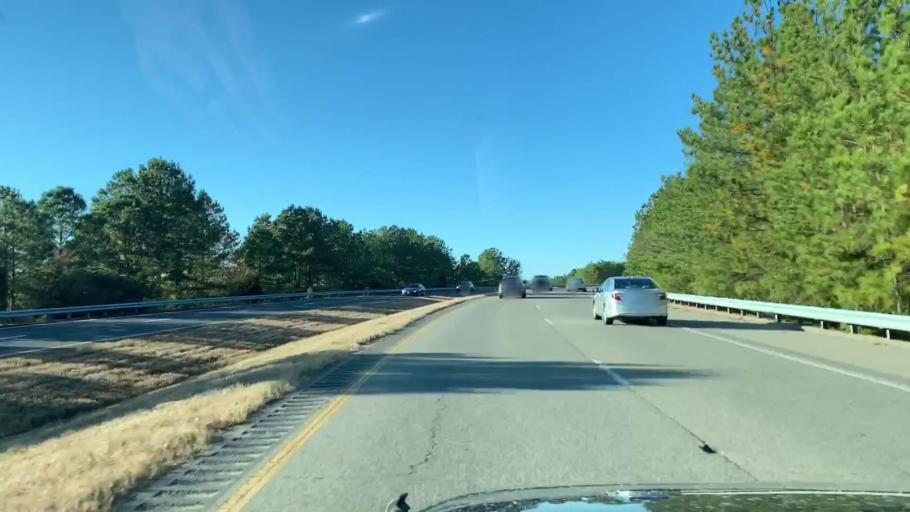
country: US
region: Virginia
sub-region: James City County
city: Williamsburg
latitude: 37.2717
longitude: -76.7508
